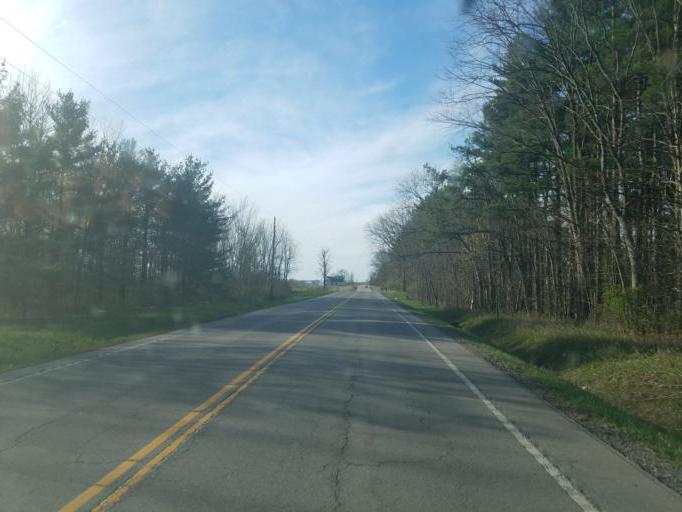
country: US
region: Ohio
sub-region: Huron County
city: New London
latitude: 41.0137
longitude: -82.4077
